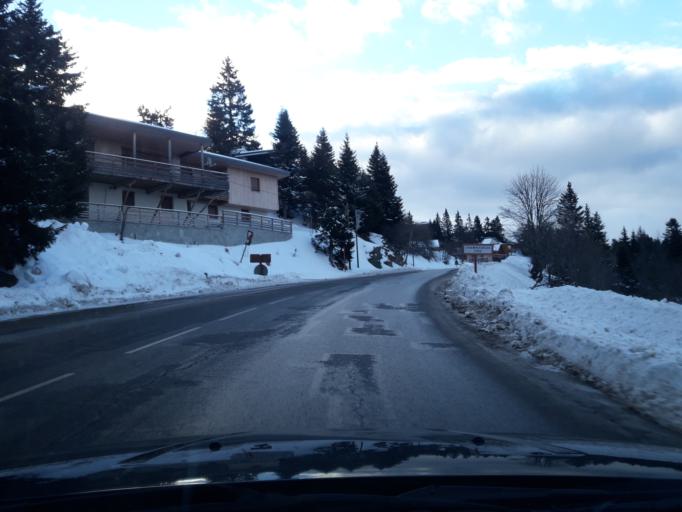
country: FR
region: Rhone-Alpes
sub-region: Departement de l'Isere
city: Vaulnaveys-le-Bas
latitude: 45.1152
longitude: 5.8740
